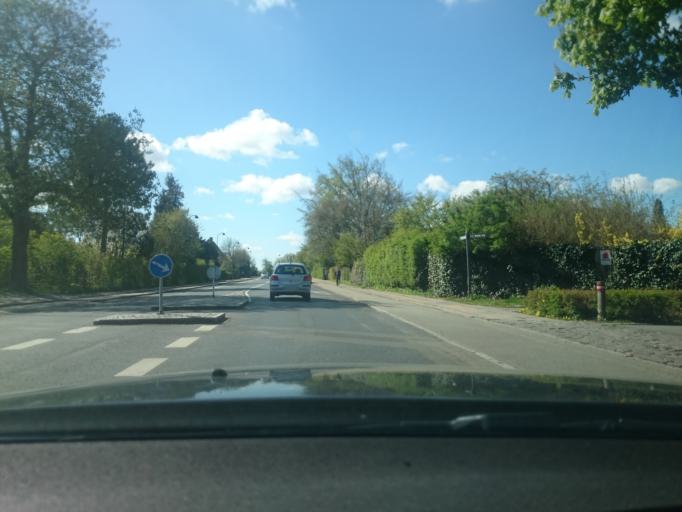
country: DK
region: Capital Region
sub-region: Lyngby-Tarbaek Kommune
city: Kongens Lyngby
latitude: 55.7558
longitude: 12.5347
